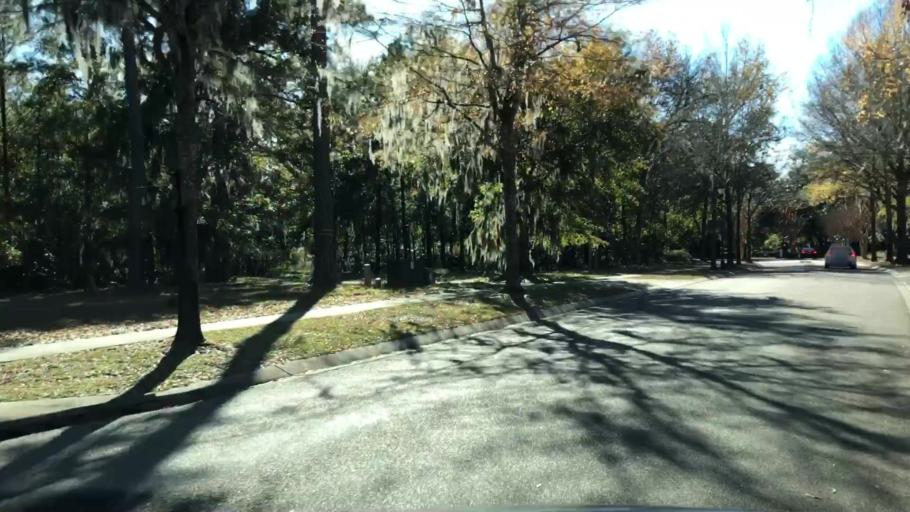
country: US
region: South Carolina
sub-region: Beaufort County
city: Bluffton
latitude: 32.2745
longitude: -80.8721
